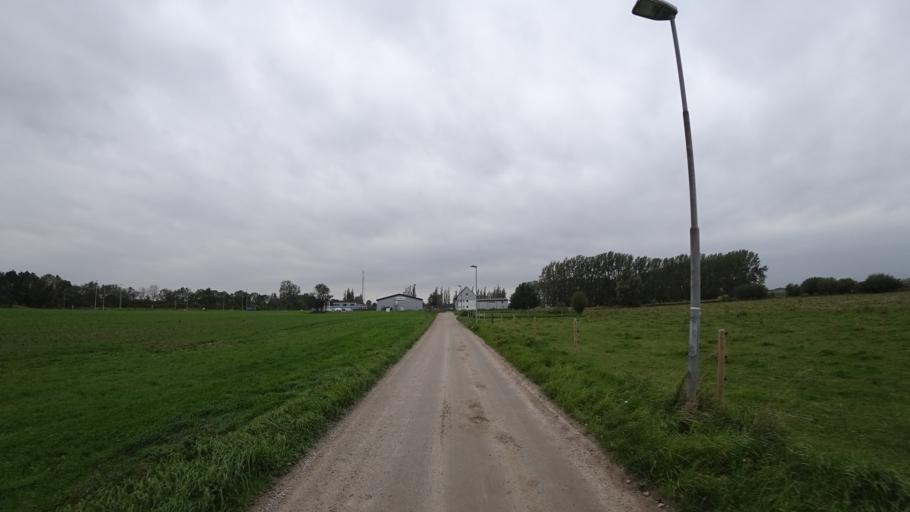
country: SE
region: Skane
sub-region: Kavlinge Kommun
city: Kaevlinge
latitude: 55.7991
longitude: 13.1318
